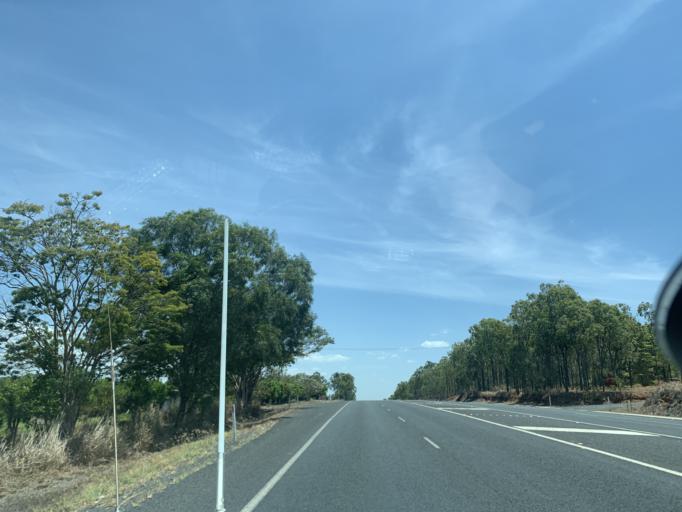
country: AU
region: Queensland
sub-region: Tablelands
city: Mareeba
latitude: -16.9857
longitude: 145.5238
